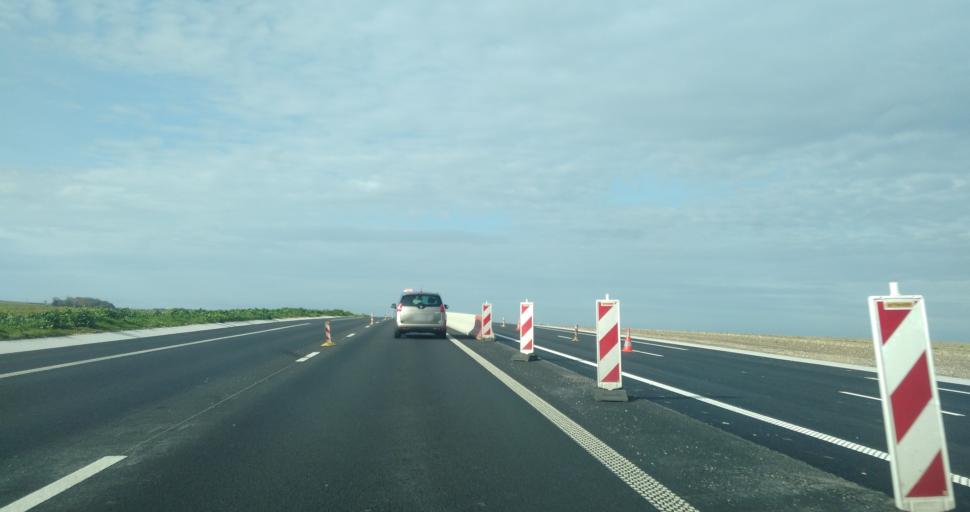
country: FR
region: Nord-Pas-de-Calais
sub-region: Departement du Pas-de-Calais
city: Aubigny-en-Artois
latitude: 50.3382
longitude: 2.6132
